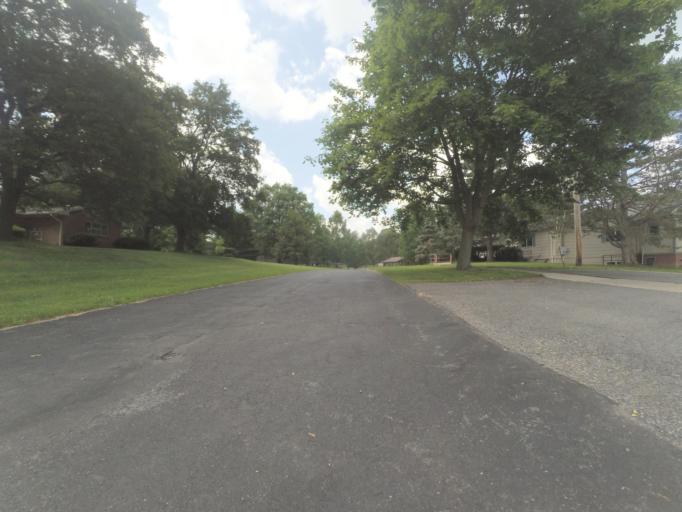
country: US
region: Pennsylvania
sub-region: Centre County
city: State College
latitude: 40.7828
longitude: -77.8407
